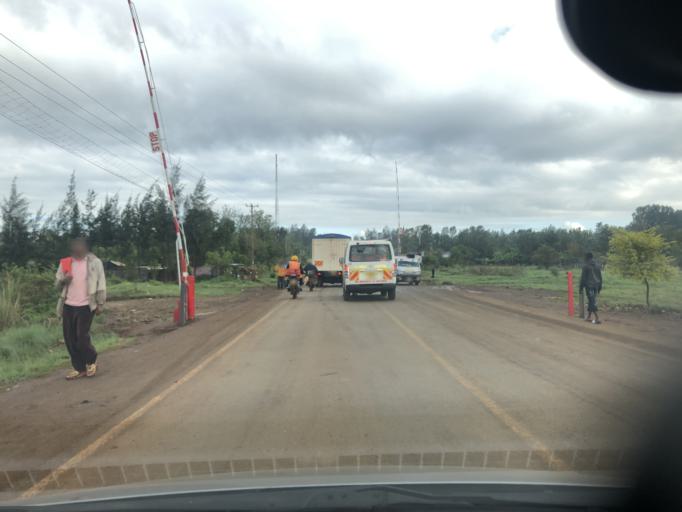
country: KE
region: Murang'a District
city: Maragua
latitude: -0.8389
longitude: 37.1381
